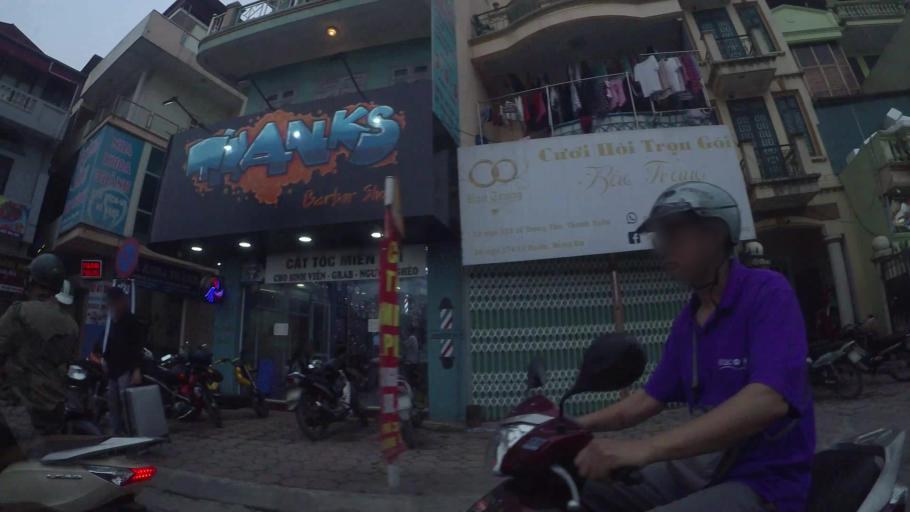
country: VN
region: Ha Noi
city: Hai BaTrung
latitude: 20.9870
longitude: 105.8354
